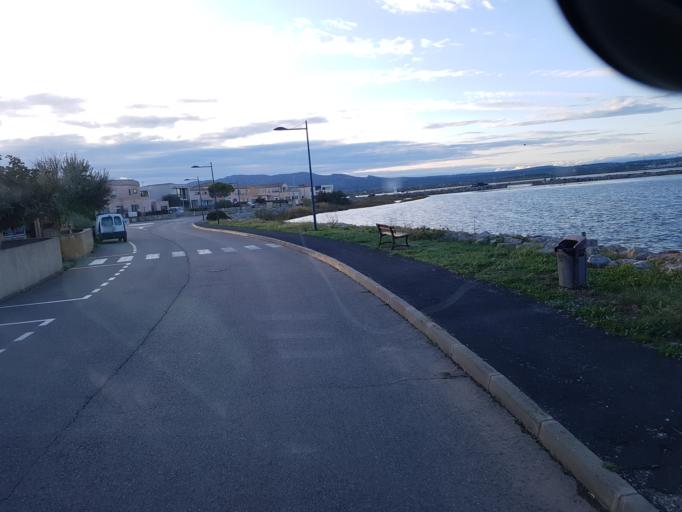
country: FR
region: Languedoc-Roussillon
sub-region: Departement de l'Aude
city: Leucate
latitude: 42.9372
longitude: 3.0289
